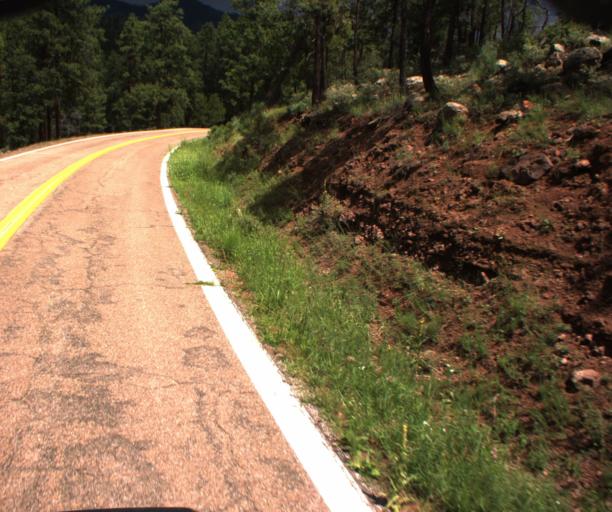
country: US
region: Arizona
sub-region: Greenlee County
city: Morenci
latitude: 33.5184
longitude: -109.3068
